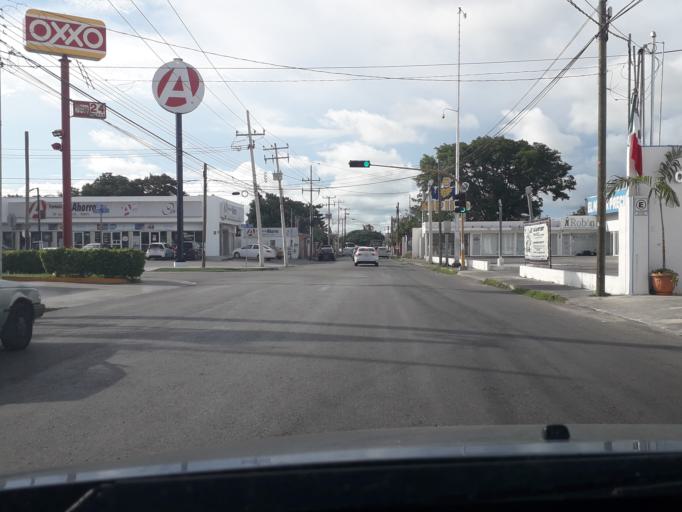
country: MX
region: Yucatan
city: Merida
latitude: 21.0022
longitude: -89.6392
